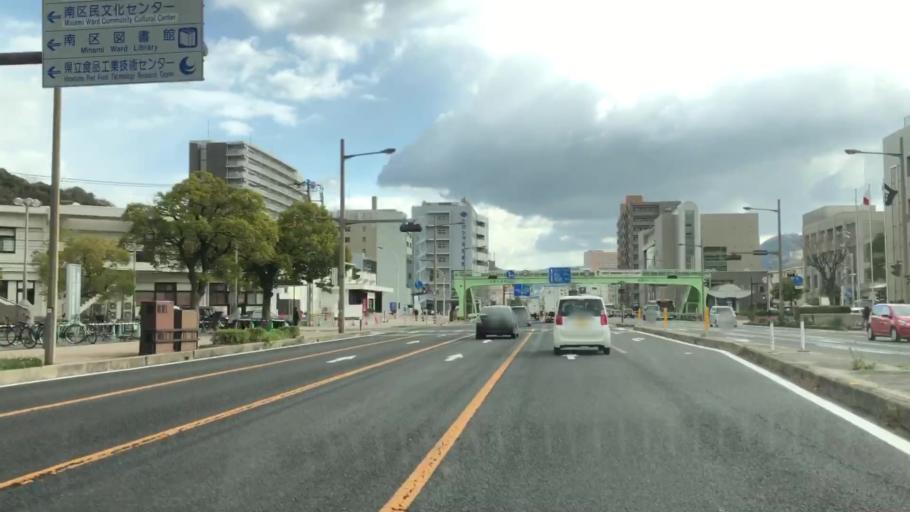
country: JP
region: Hiroshima
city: Hiroshima-shi
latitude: 34.3804
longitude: 132.4686
